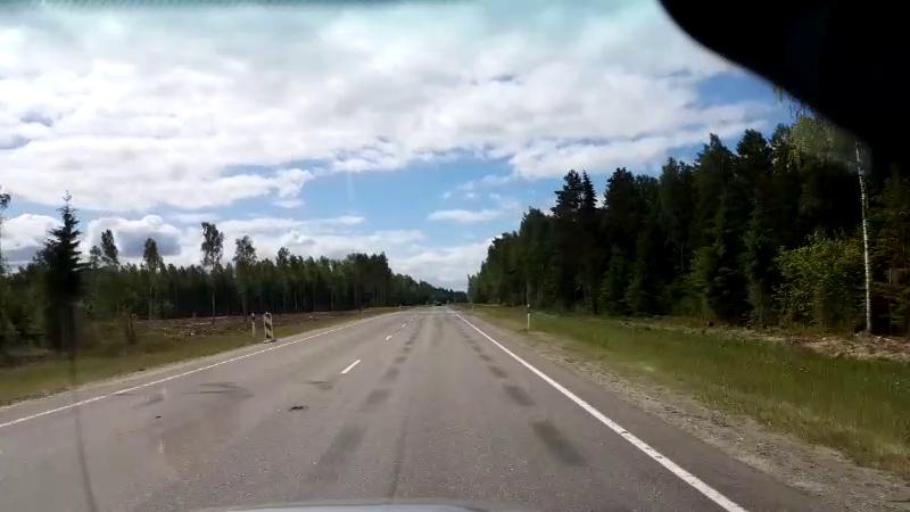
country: LV
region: Salacgrivas
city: Ainazi
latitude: 58.0313
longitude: 24.5048
